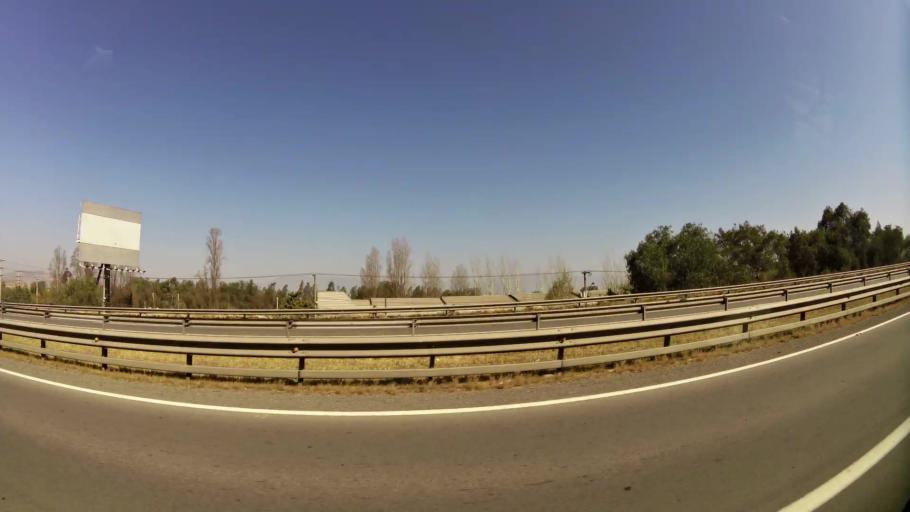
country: CL
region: Santiago Metropolitan
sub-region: Provincia de Chacabuco
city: Chicureo Abajo
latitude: -33.3434
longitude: -70.6942
